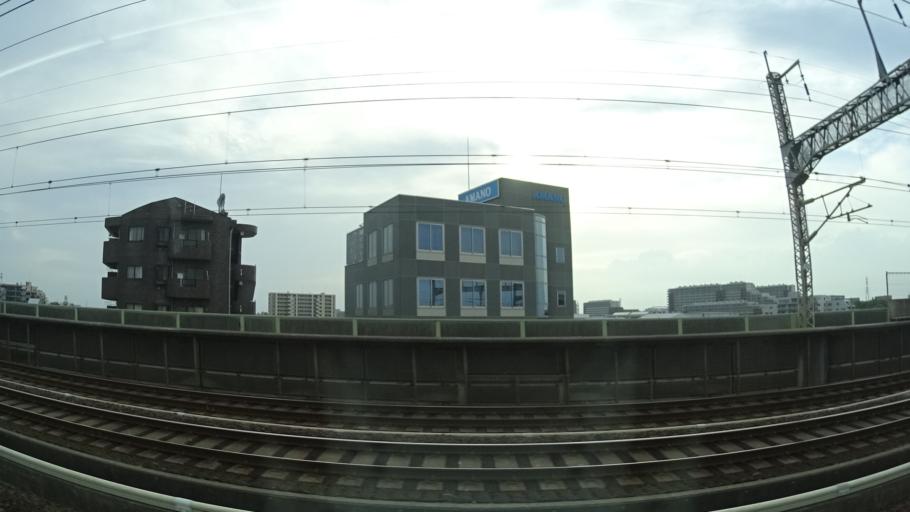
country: JP
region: Saitama
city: Ageoshimo
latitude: 35.9326
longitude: 139.6164
